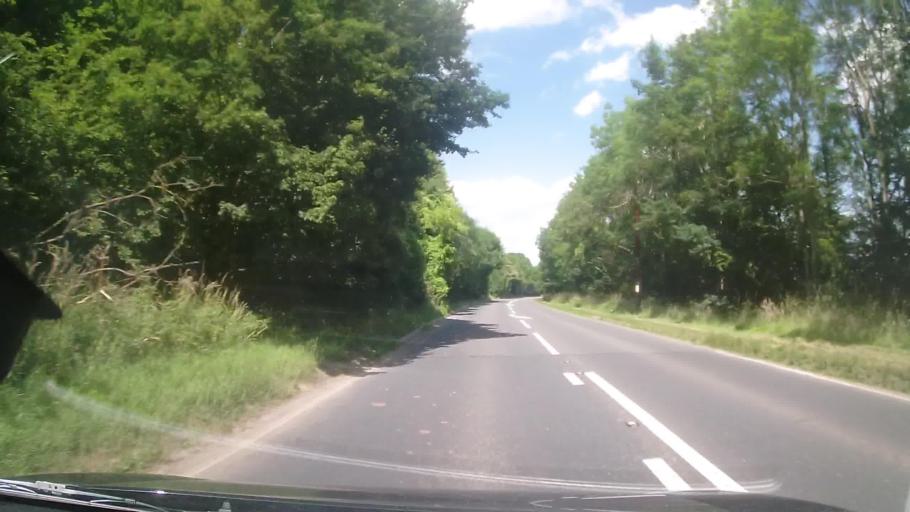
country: GB
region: England
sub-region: Herefordshire
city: Ocle Pychard
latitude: 52.0874
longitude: -2.5856
